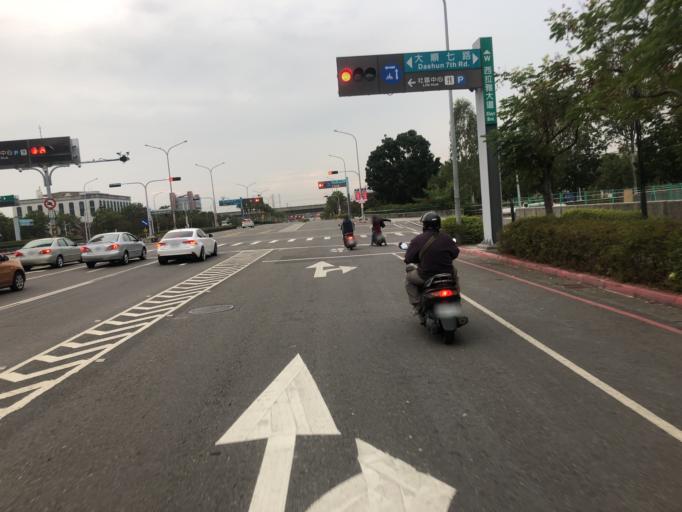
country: TW
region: Taiwan
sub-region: Tainan
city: Tainan
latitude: 23.1040
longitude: 120.2878
